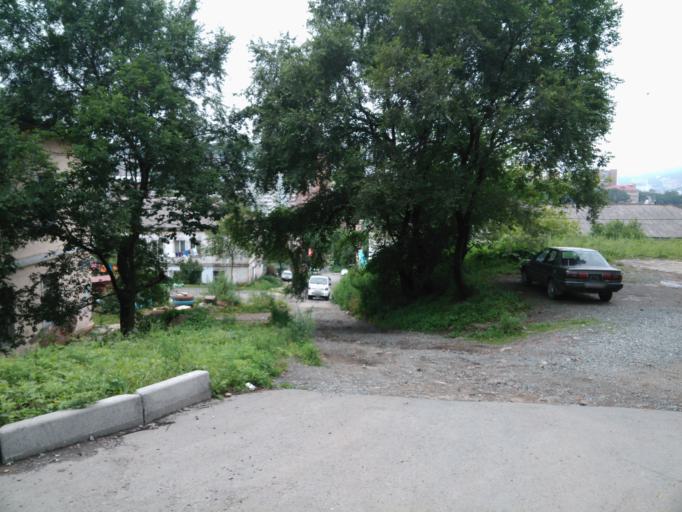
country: RU
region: Primorskiy
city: Vladivostok
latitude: 43.0922
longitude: 131.9591
